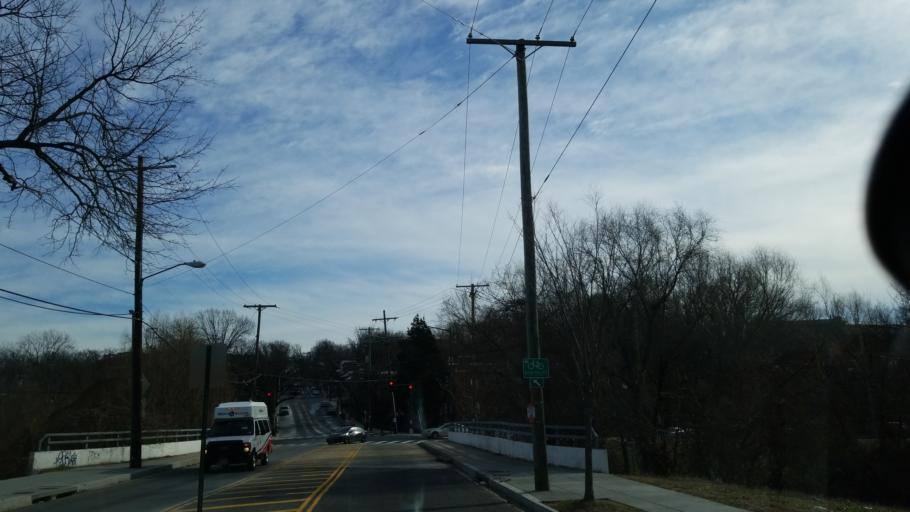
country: US
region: Maryland
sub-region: Prince George's County
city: Glassmanor
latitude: 38.8310
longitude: -77.0044
